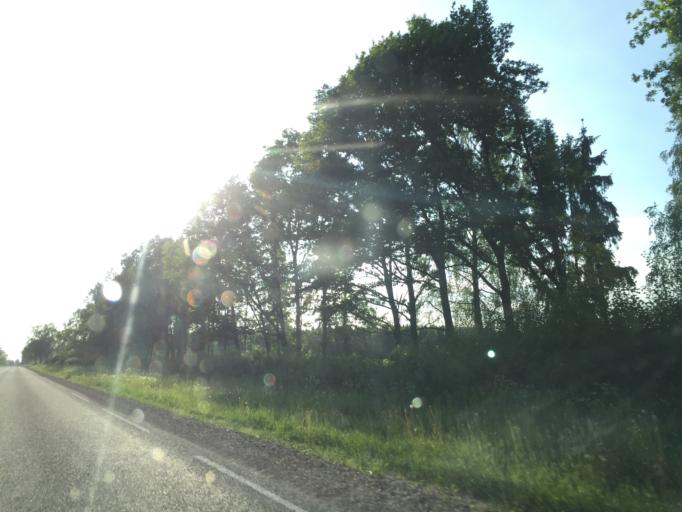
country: LV
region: Rundales
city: Pilsrundale
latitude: 56.4315
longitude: 23.9832
